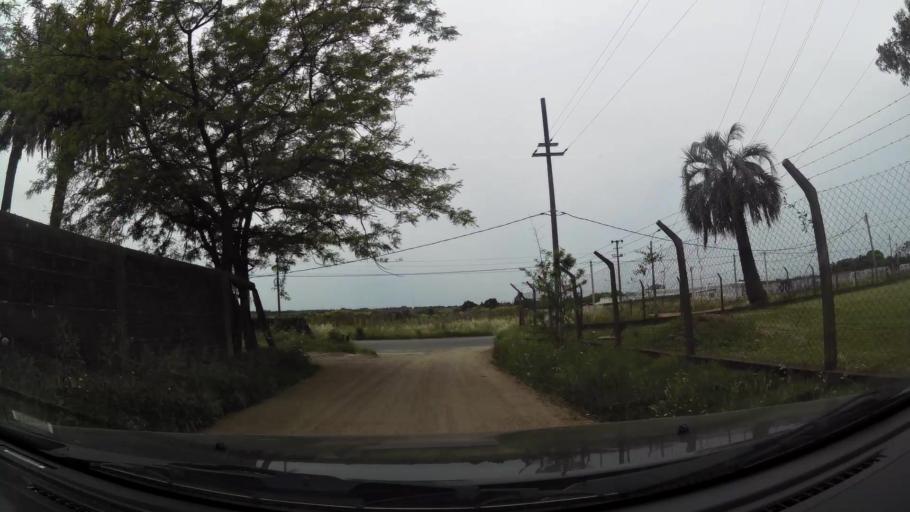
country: UY
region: Canelones
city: La Paz
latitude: -34.7471
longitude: -56.2241
